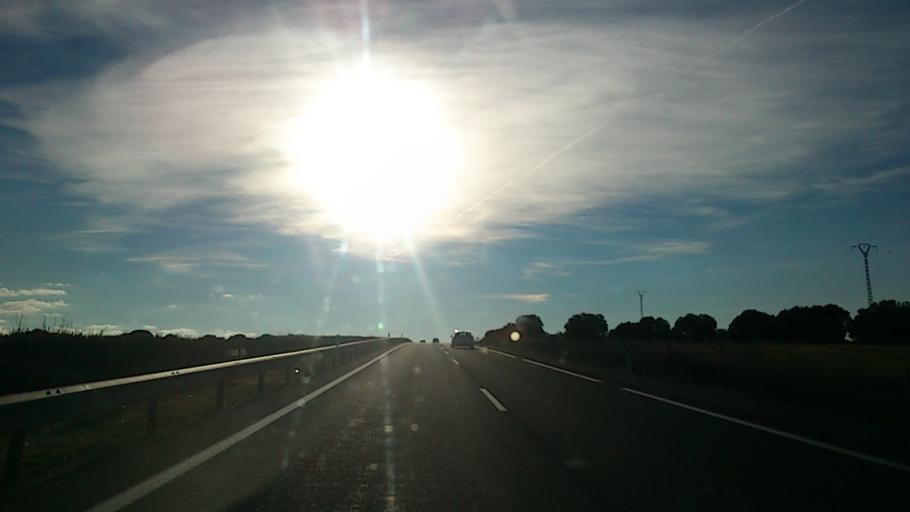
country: ES
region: Castille-La Mancha
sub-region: Provincia de Guadalajara
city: Mirabueno
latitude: 40.9431
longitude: -2.6963
